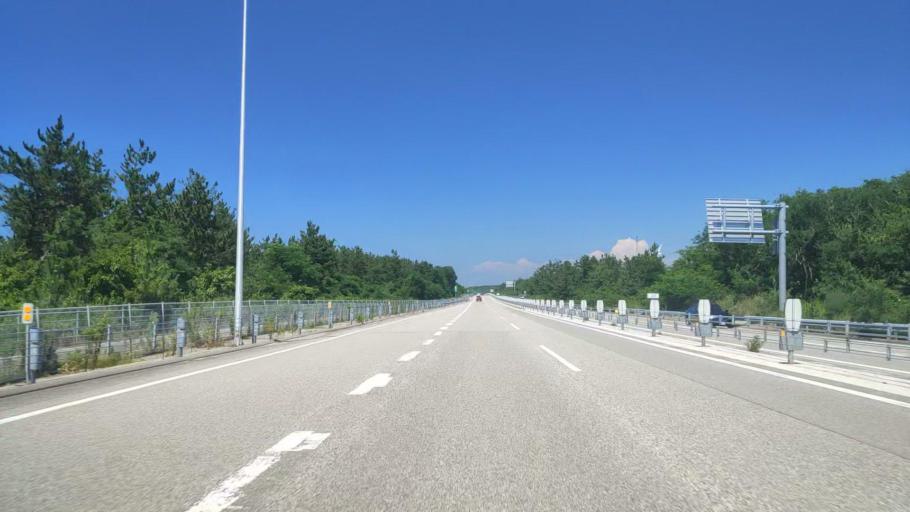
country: JP
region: Ishikawa
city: Kanazawa-shi
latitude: 36.6545
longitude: 136.6374
